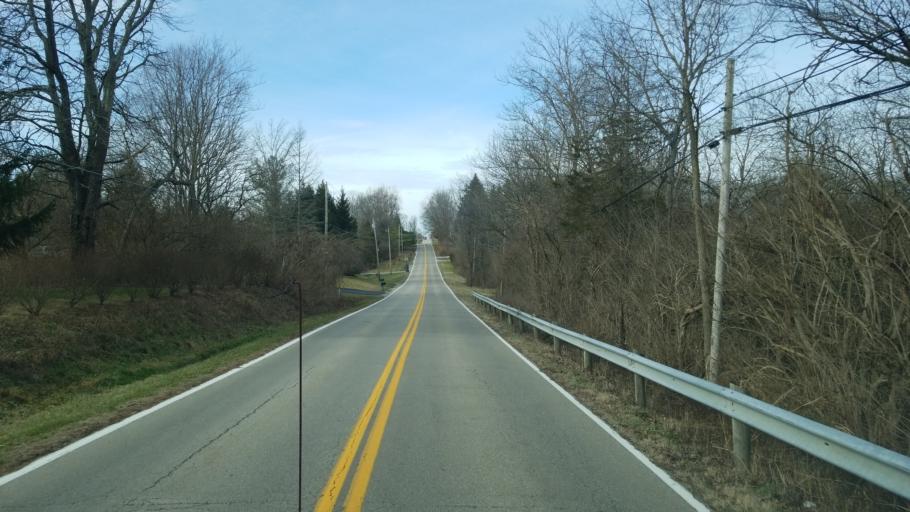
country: US
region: Ohio
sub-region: Warren County
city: Lebanon
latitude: 39.4285
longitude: -84.1335
